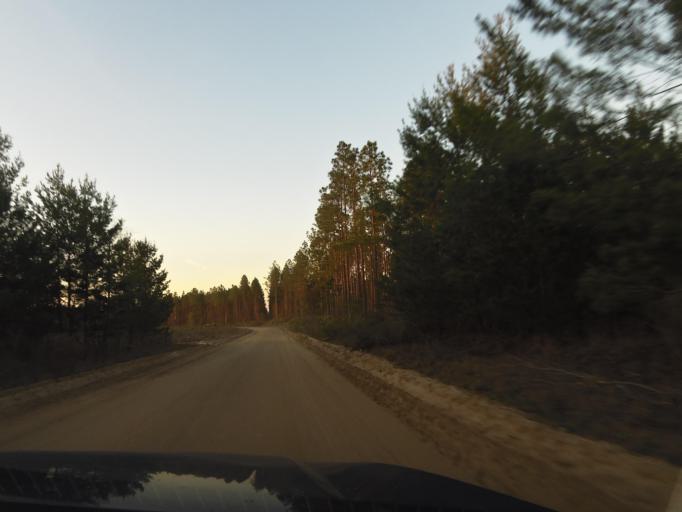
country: US
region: Florida
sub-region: Clay County
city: Green Cove Springs
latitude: 29.9272
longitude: -81.7809
